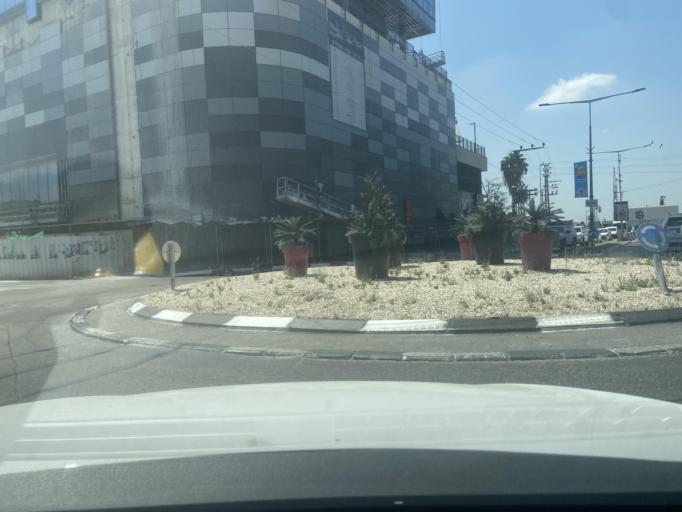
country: IL
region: Central District
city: Yehud
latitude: 32.0265
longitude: 34.8988
